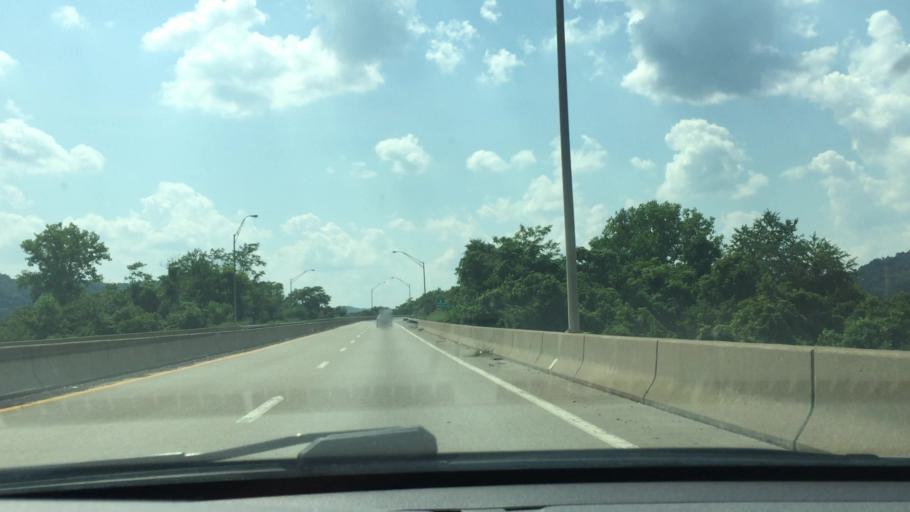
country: US
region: West Virginia
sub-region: Marshall County
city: Moundsville
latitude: 39.9141
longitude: -80.7578
